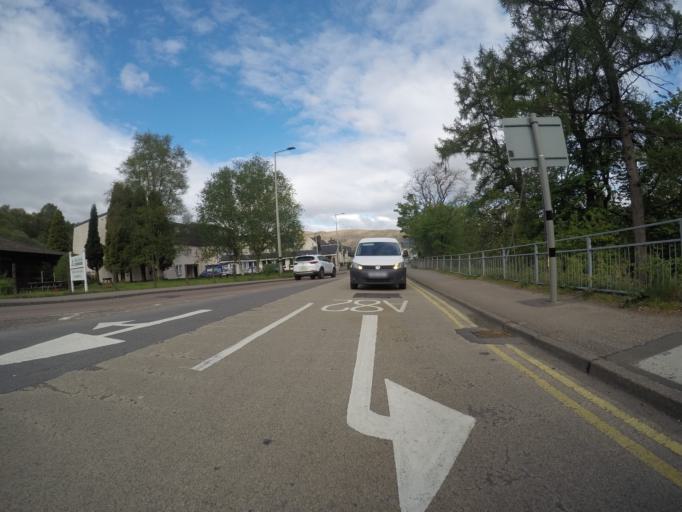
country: GB
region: Scotland
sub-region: Highland
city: Fort William
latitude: 56.8215
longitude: -5.0948
